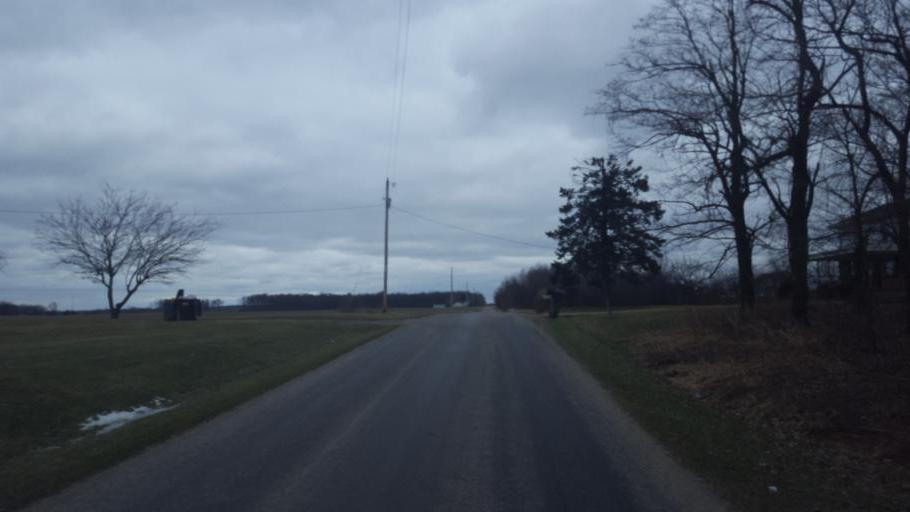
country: US
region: Ohio
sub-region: Crawford County
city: Galion
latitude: 40.6678
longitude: -82.7359
